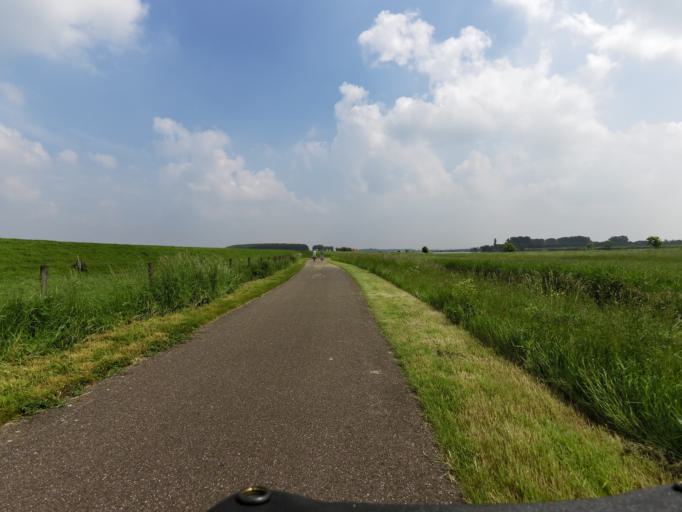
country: NL
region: South Holland
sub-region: Gemeente Spijkenisse
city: Spijkenisse
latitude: 51.8066
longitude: 4.2709
